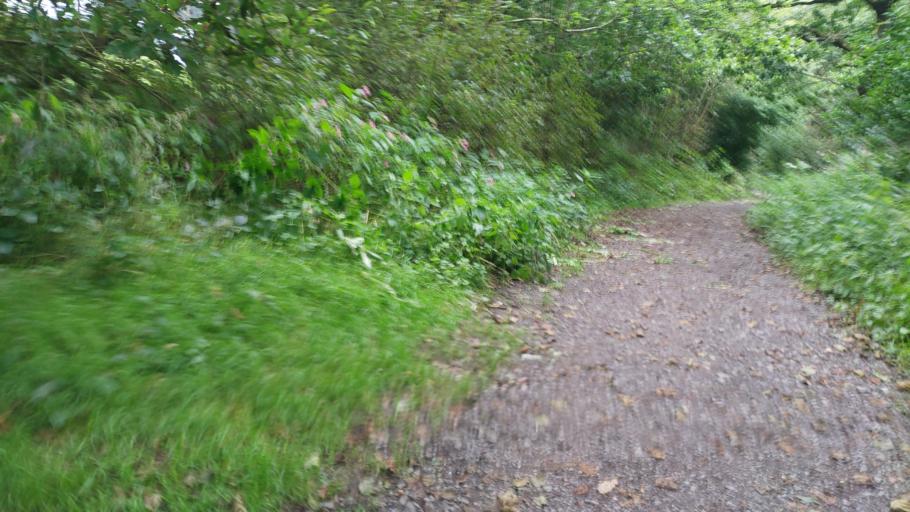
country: GB
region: England
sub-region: Lancashire
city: Clayton-le-Woods
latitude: 53.7109
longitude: -2.6483
